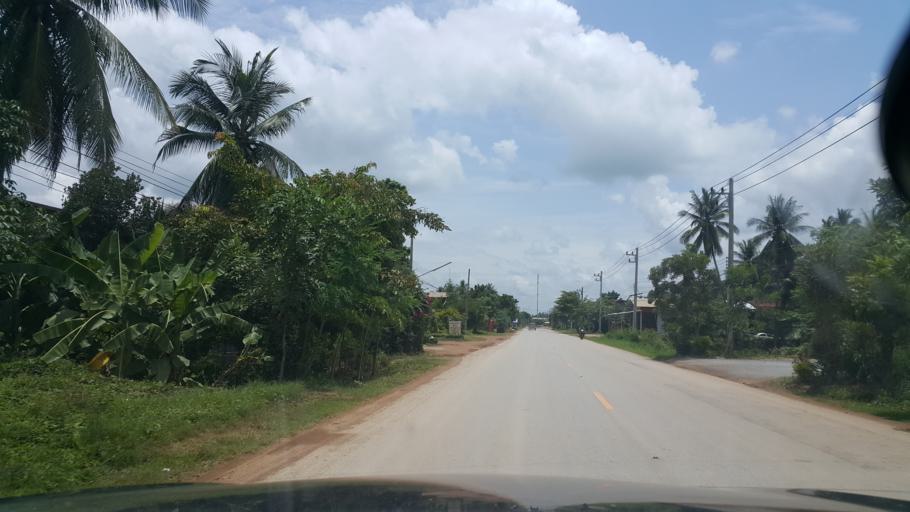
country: TH
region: Sukhothai
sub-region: Amphoe Si Satchanalai
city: Si Satchanalai
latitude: 17.4438
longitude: 99.7260
